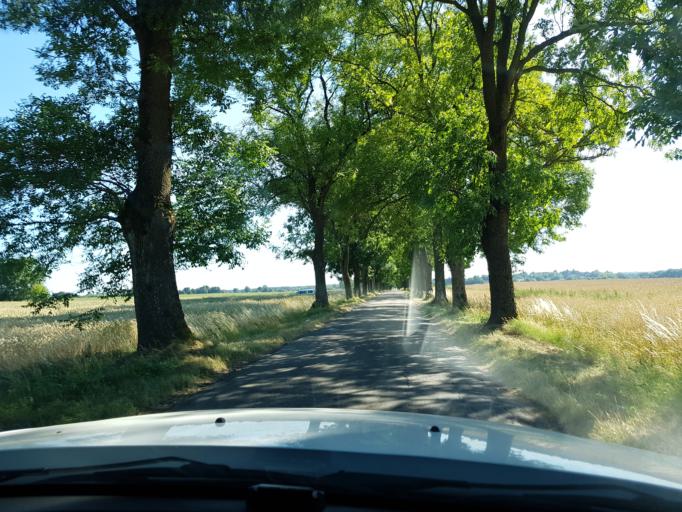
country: PL
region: West Pomeranian Voivodeship
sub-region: Powiat swidwinski
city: Slawoborze
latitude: 53.8288
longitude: 15.6931
